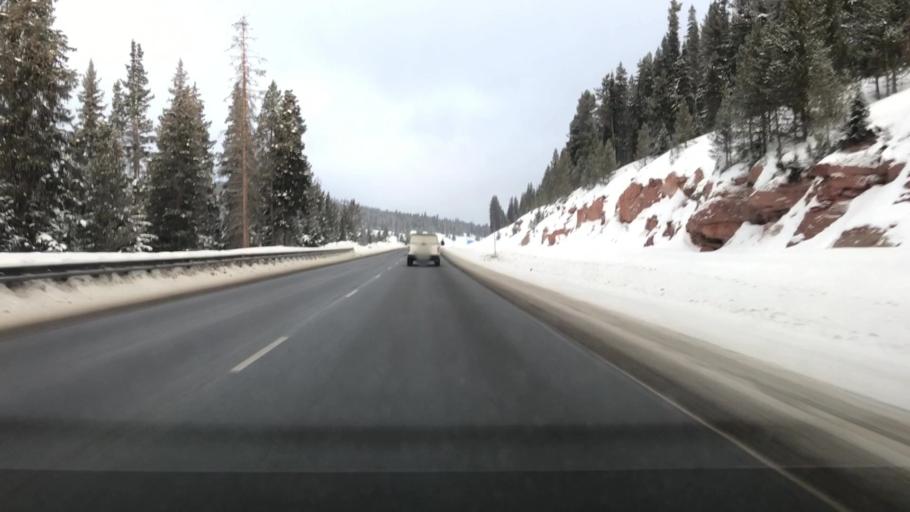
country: US
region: Colorado
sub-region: Summit County
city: Frisco
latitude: 39.5215
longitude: -106.2129
